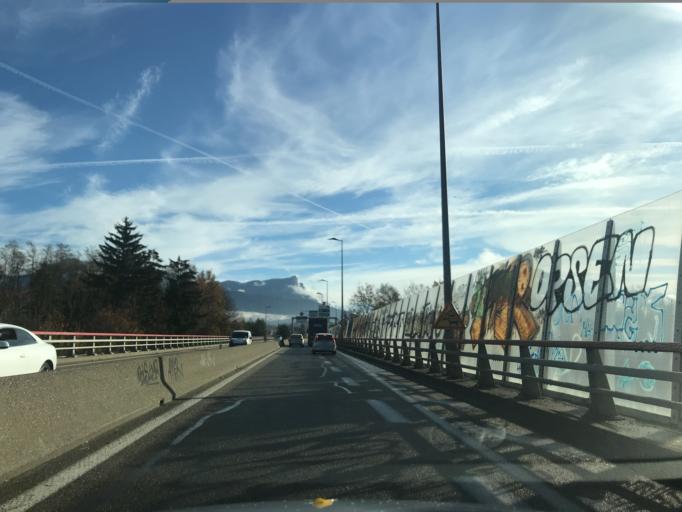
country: FR
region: Rhone-Alpes
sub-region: Departement de la Haute-Savoie
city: Metz-Tessy
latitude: 45.9378
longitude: 6.1124
